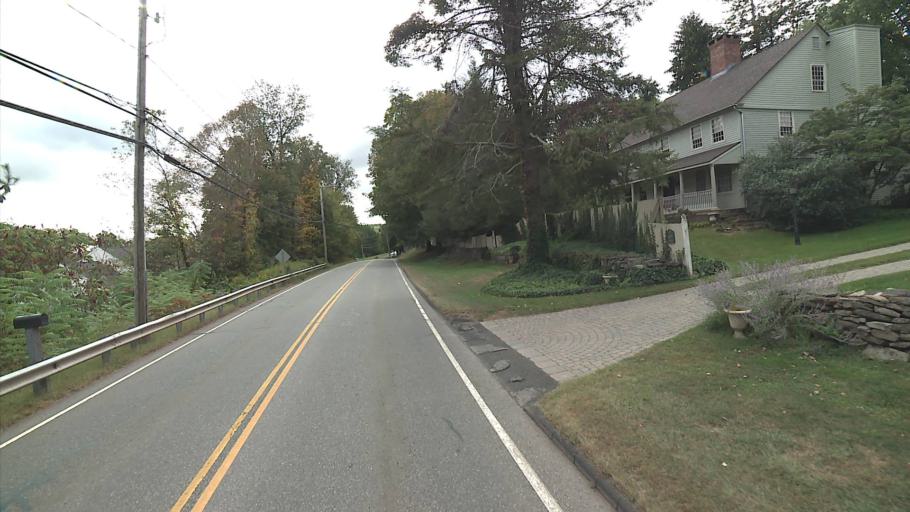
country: US
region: Connecticut
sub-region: Middlesex County
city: Durham
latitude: 41.5025
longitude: -72.7166
